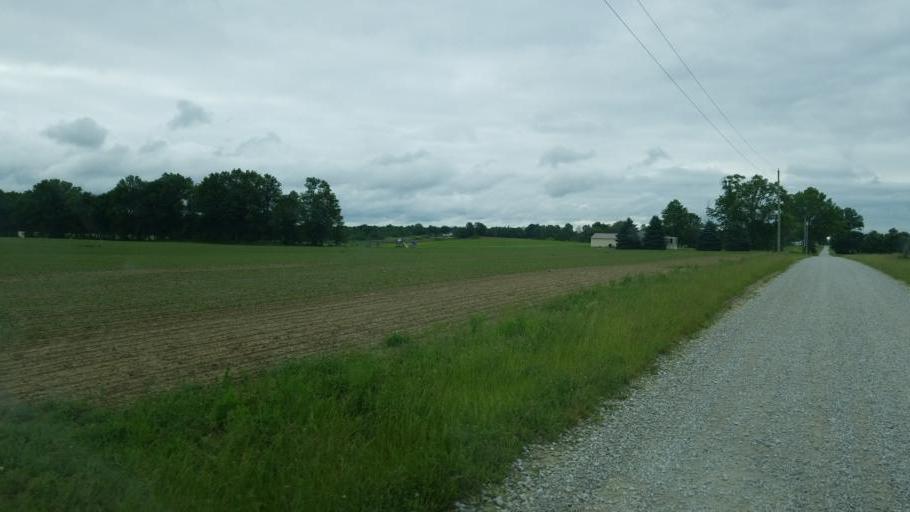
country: US
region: Ohio
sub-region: Morrow County
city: Mount Gilead
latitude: 40.5232
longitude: -82.7781
